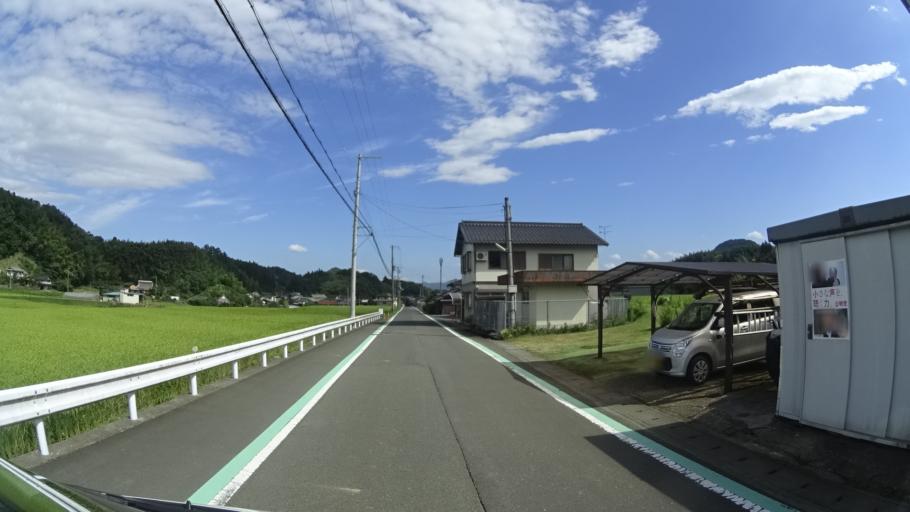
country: JP
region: Kyoto
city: Fukuchiyama
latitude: 35.3301
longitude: 135.1742
